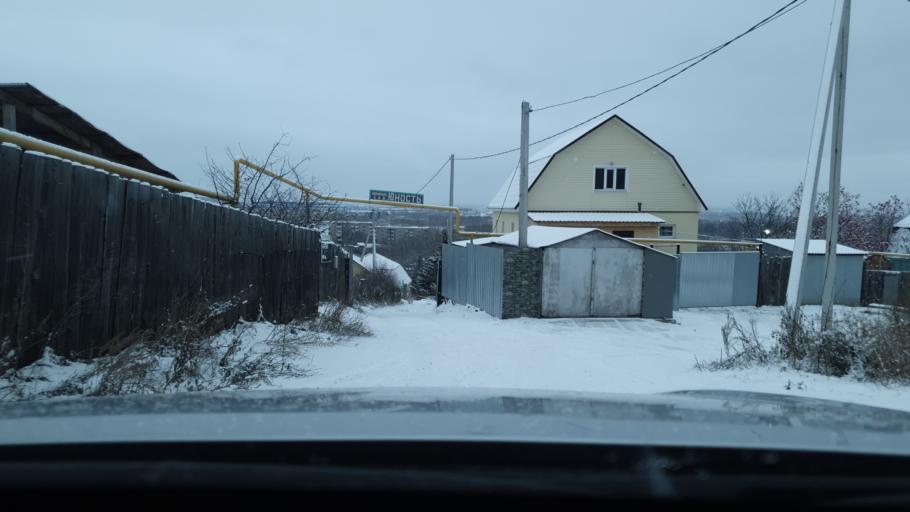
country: RU
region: Sverdlovsk
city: Istok
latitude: 56.7437
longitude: 60.7027
